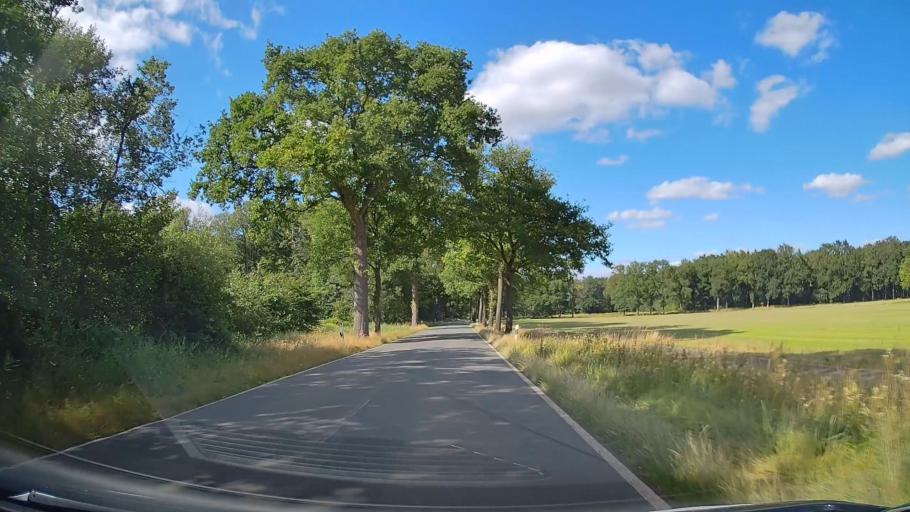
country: DE
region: Lower Saxony
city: Menslage
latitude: 52.6485
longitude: 7.8109
